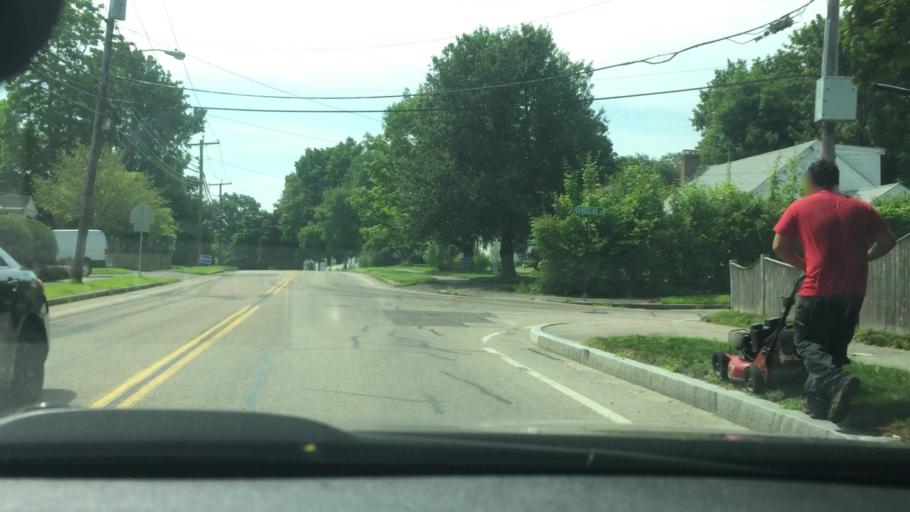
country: US
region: Massachusetts
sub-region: Norfolk County
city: Needham
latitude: 42.3059
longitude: -71.2363
